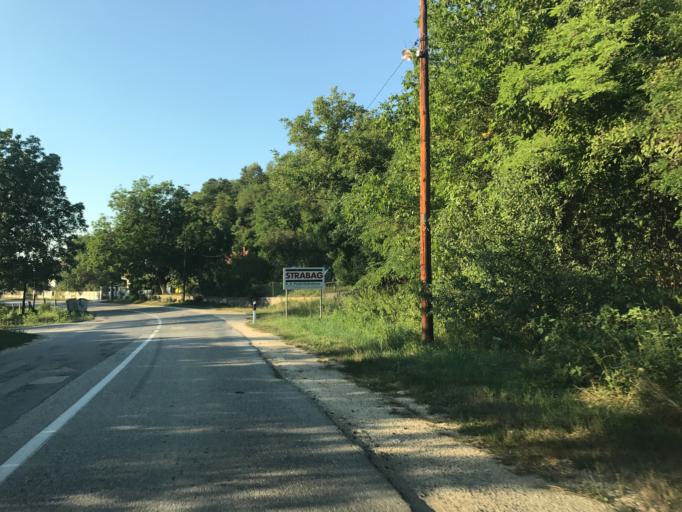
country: RO
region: Mehedinti
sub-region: Comuna Svinita
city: Svinita
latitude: 44.3491
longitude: 22.1795
